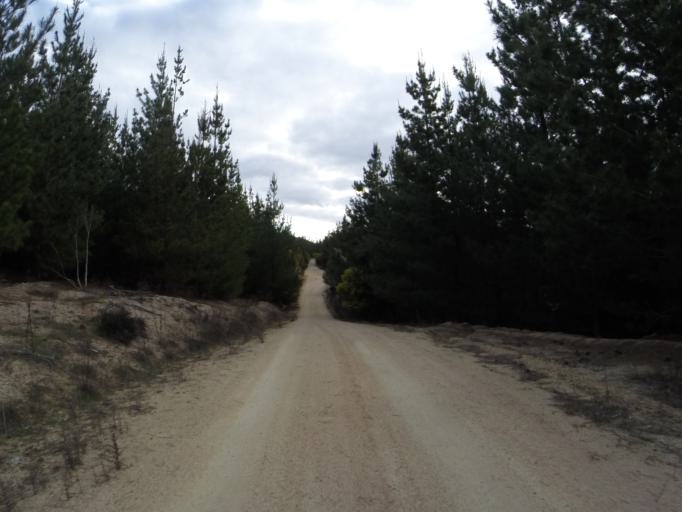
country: AU
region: Australian Capital Territory
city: Macquarie
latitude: -35.3478
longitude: 148.9472
